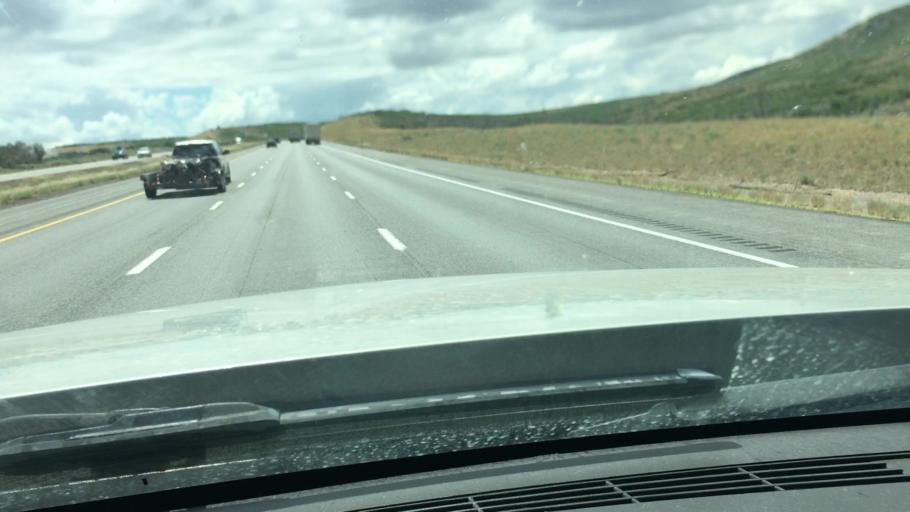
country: US
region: Utah
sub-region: Beaver County
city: Beaver
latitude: 38.4962
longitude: -112.6170
